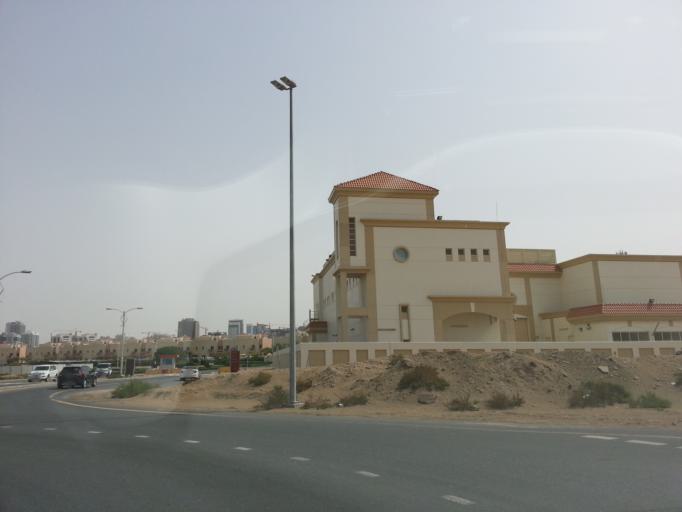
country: AE
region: Dubai
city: Dubai
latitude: 25.0337
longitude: 55.2057
